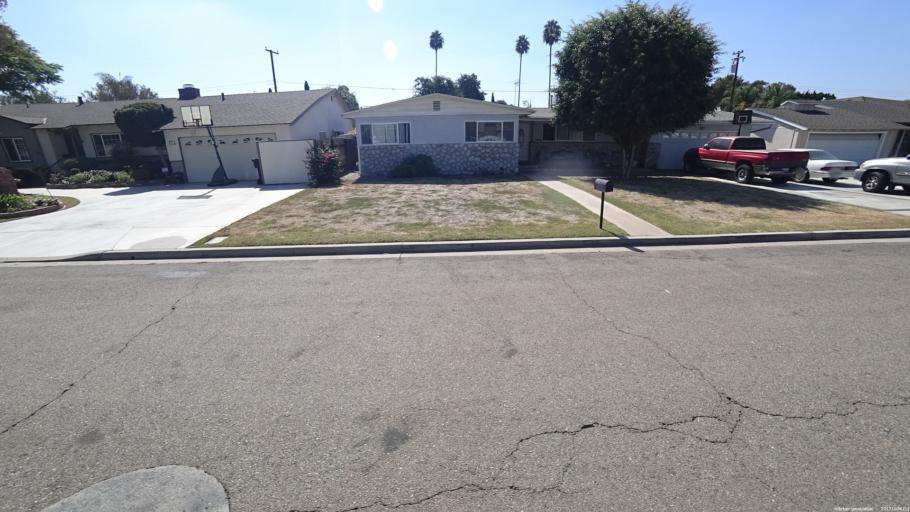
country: US
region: California
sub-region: Orange County
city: Garden Grove
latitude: 33.7926
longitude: -117.9559
